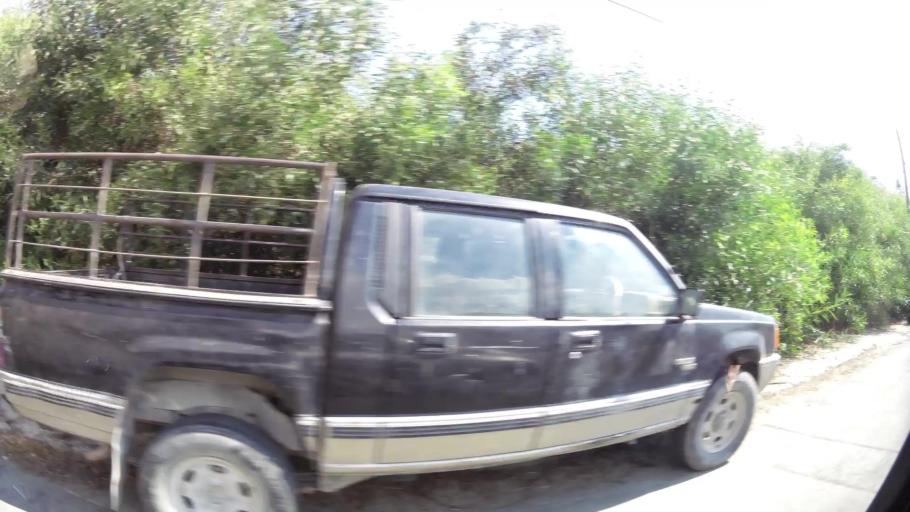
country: CY
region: Larnaka
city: Larnaca
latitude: 34.9092
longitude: 33.6231
